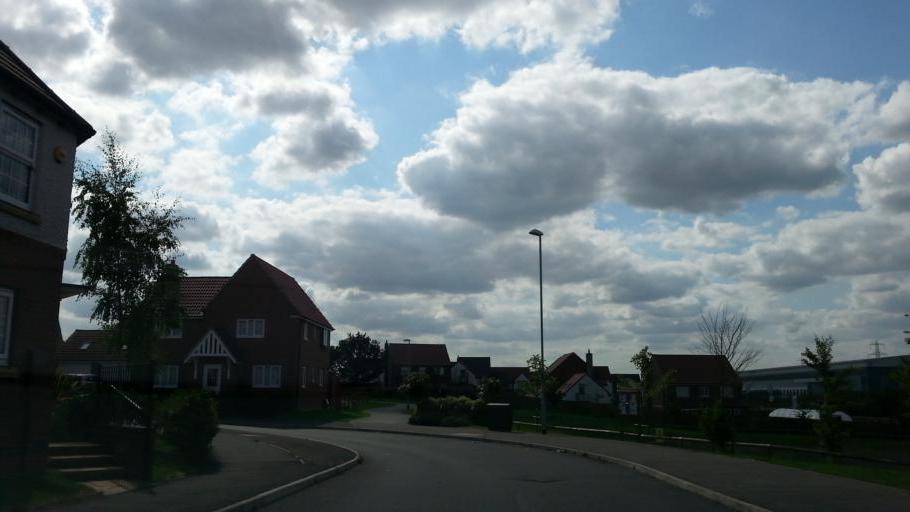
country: GB
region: England
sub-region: Leicestershire
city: Glenfield
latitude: 52.6463
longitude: -1.2126
